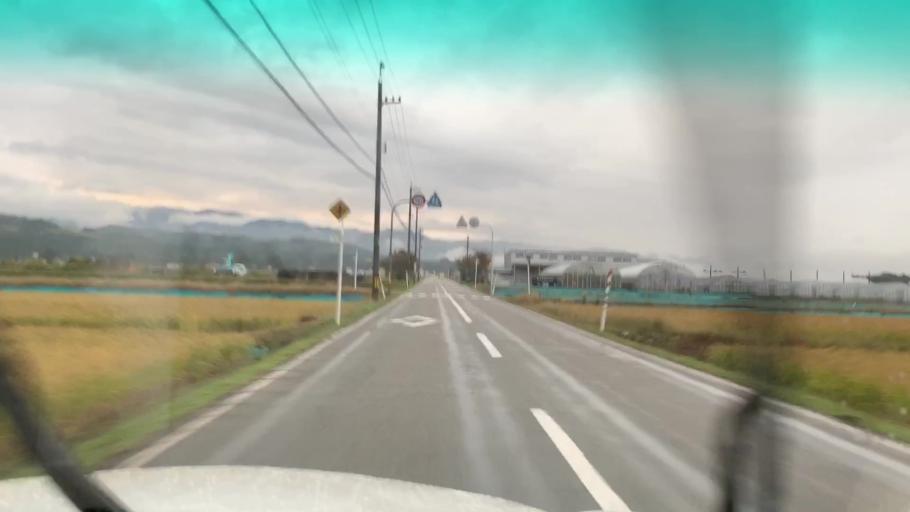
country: JP
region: Toyama
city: Kamiichi
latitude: 36.6395
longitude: 137.3285
